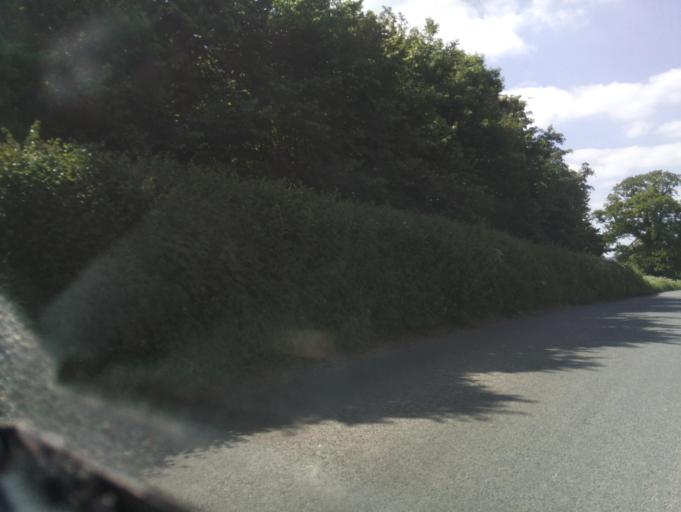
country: GB
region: England
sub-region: Wiltshire
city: Huish
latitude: 51.3539
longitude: -1.8055
